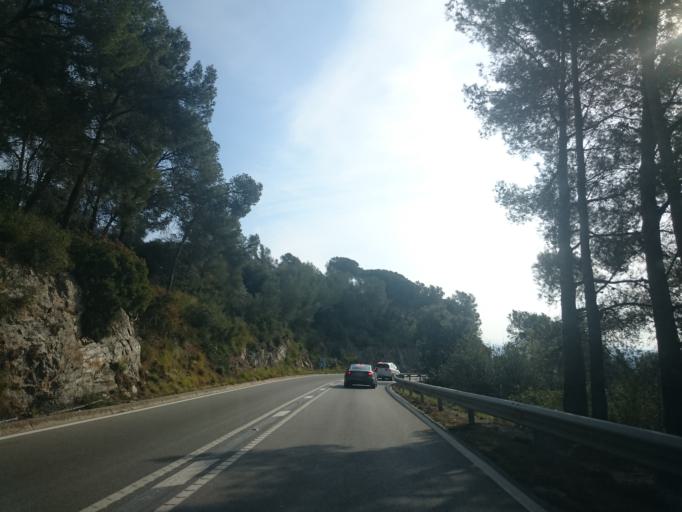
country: ES
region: Catalonia
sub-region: Provincia de Barcelona
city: Gava
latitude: 41.3119
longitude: 1.9721
